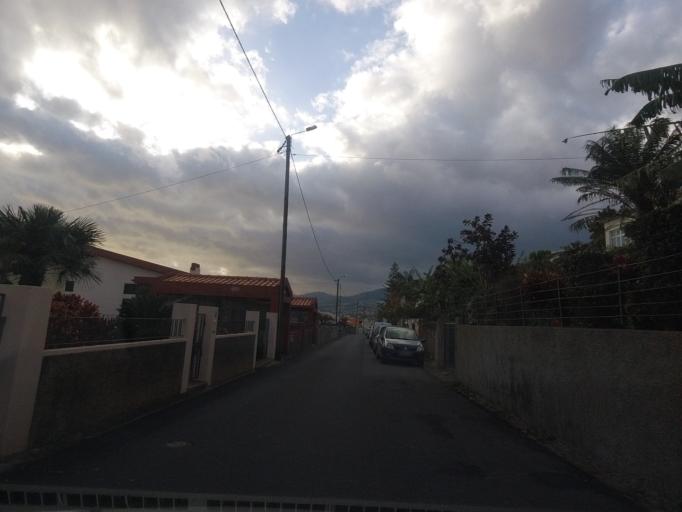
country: PT
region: Madeira
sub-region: Funchal
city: Nossa Senhora do Monte
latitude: 32.6565
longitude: -16.8884
